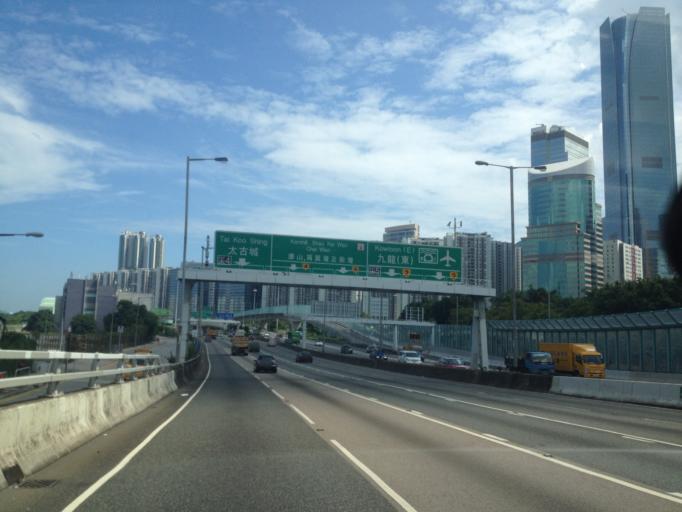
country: HK
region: Kowloon City
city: Kowloon
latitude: 22.2916
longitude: 114.2111
